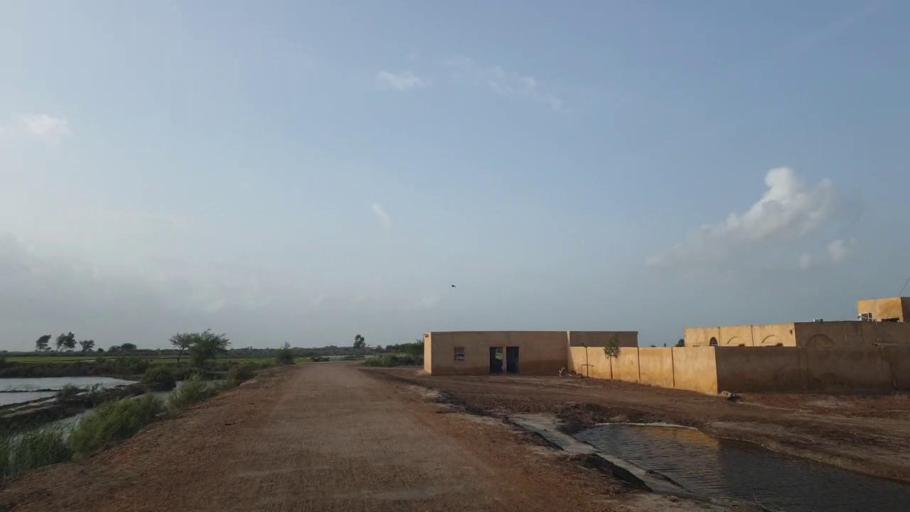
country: PK
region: Sindh
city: Tando Bago
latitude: 24.6617
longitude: 69.1120
